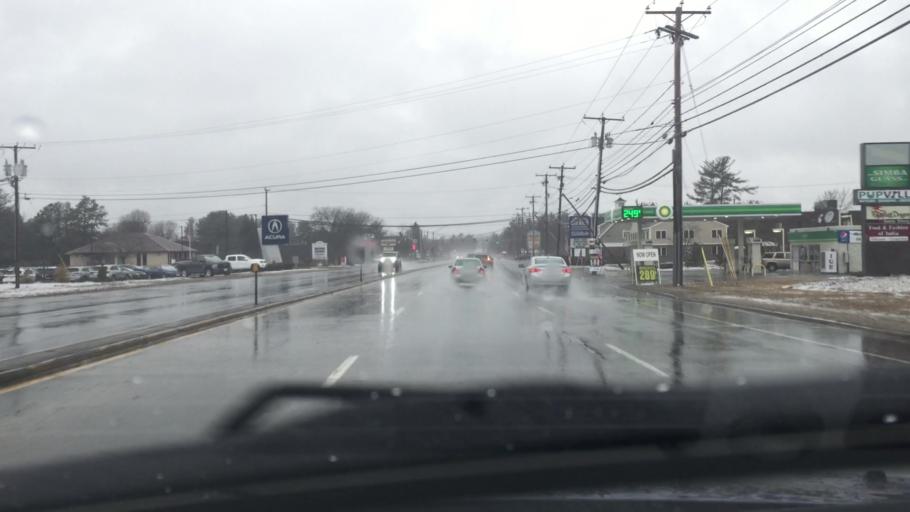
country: US
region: New Hampshire
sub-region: Hillsborough County
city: Nashua
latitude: 42.7914
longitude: -71.5203
